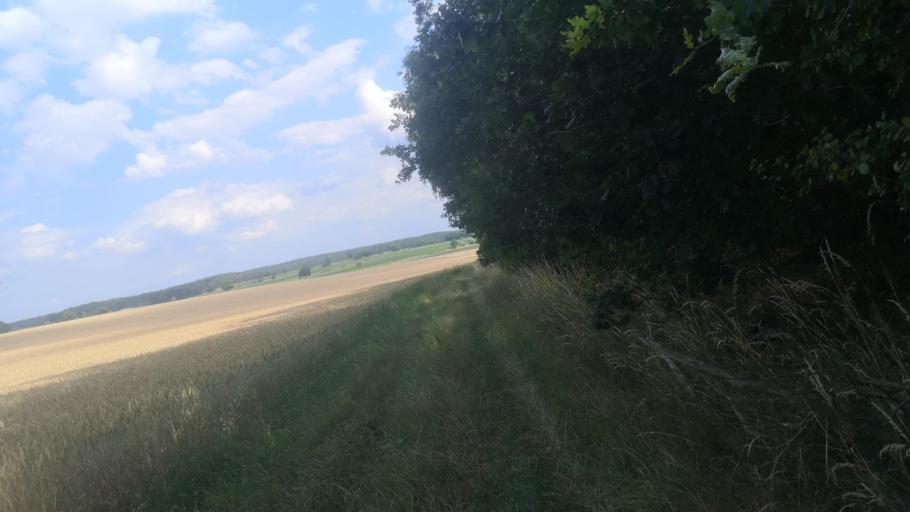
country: DE
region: Lower Saxony
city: Dahlem
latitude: 53.2204
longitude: 10.7455
